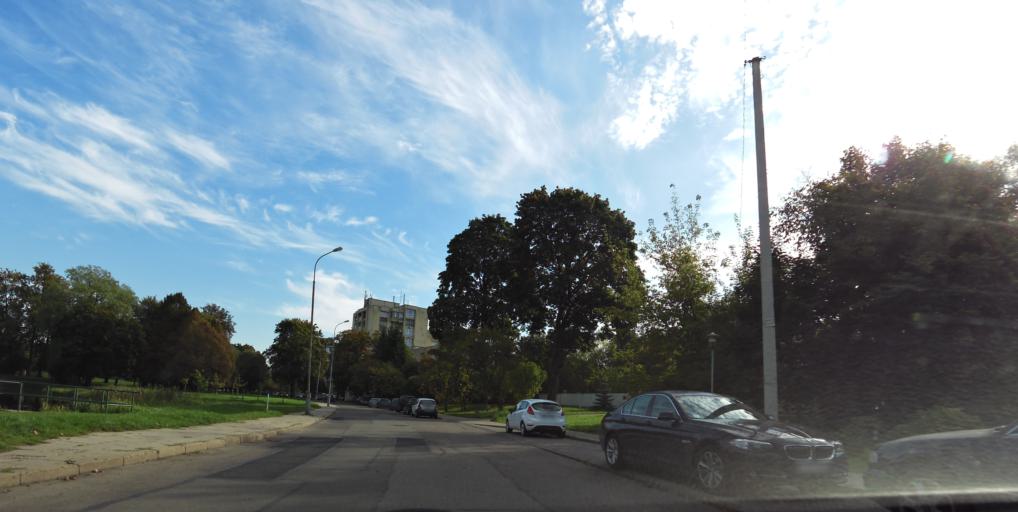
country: LT
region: Vilnius County
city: Seskine
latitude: 54.6941
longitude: 25.2398
